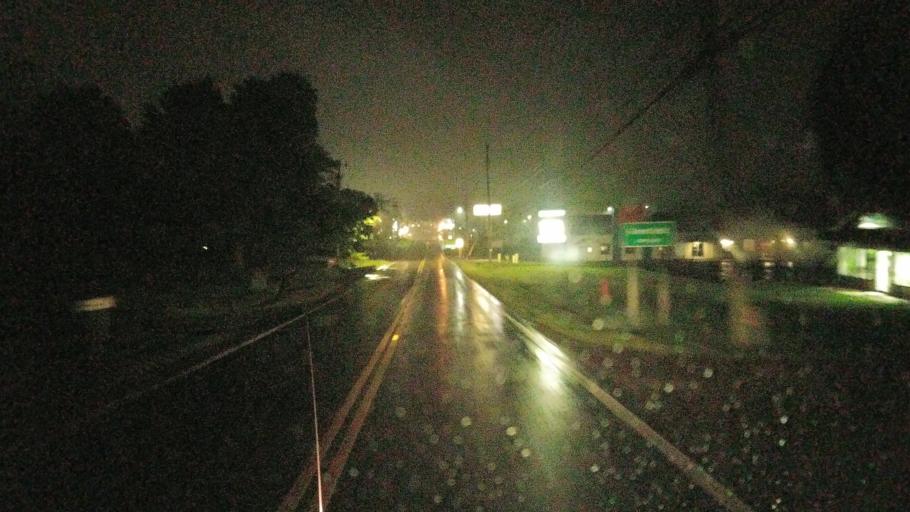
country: US
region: Ohio
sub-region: Highland County
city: Greenfield
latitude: 39.3475
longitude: -83.4042
